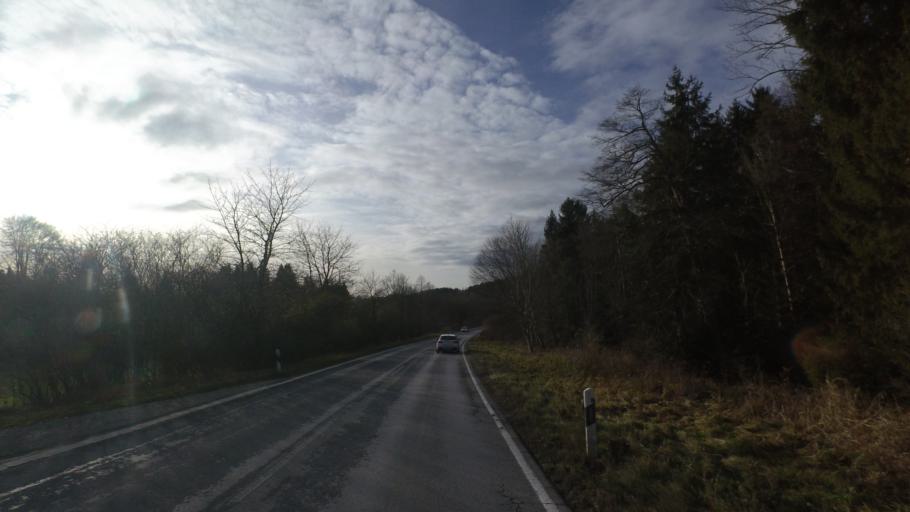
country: DE
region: Bavaria
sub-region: Upper Bavaria
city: Bad Endorf
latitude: 47.9008
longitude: 12.2661
